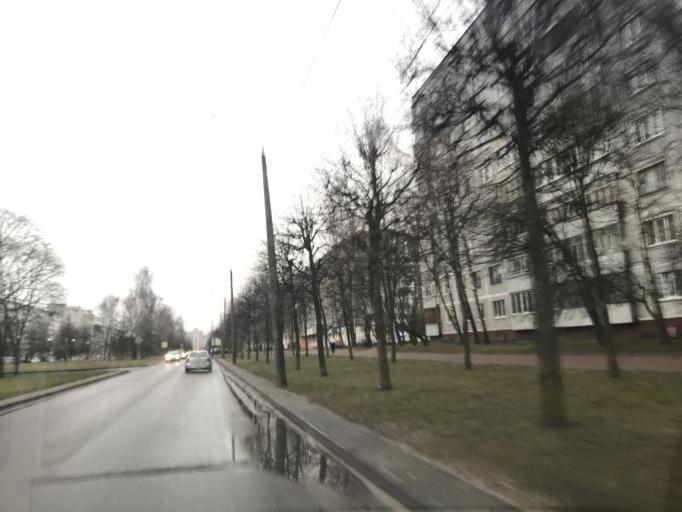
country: BY
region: Mogilev
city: Mahilyow
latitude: 53.8714
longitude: 30.3357
